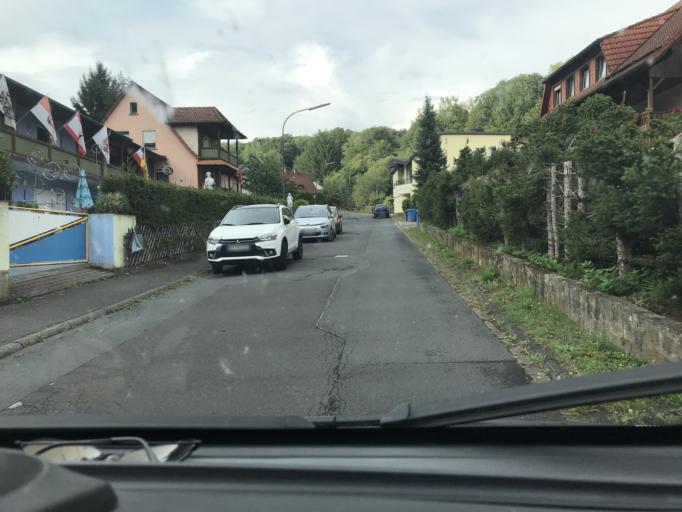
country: DE
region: Bavaria
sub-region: Regierungsbezirk Unterfranken
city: Bad Bruckenau
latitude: 50.3159
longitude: 9.7870
